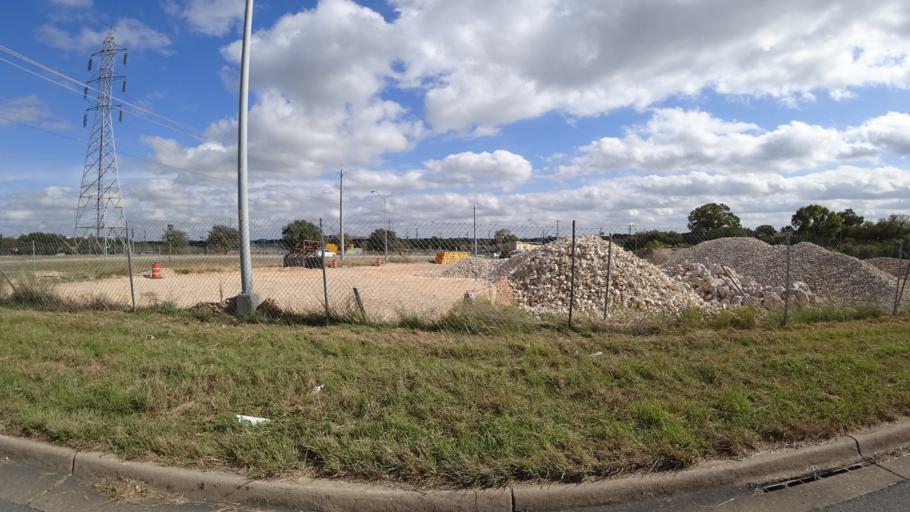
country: US
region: Texas
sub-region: Travis County
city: Wells Branch
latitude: 30.4075
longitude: -97.7157
